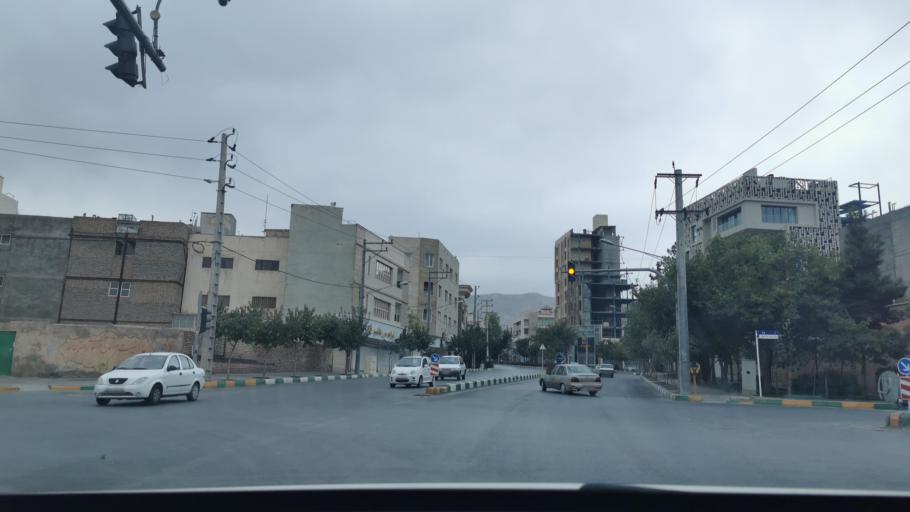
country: IR
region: Razavi Khorasan
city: Mashhad
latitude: 36.3059
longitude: 59.5004
